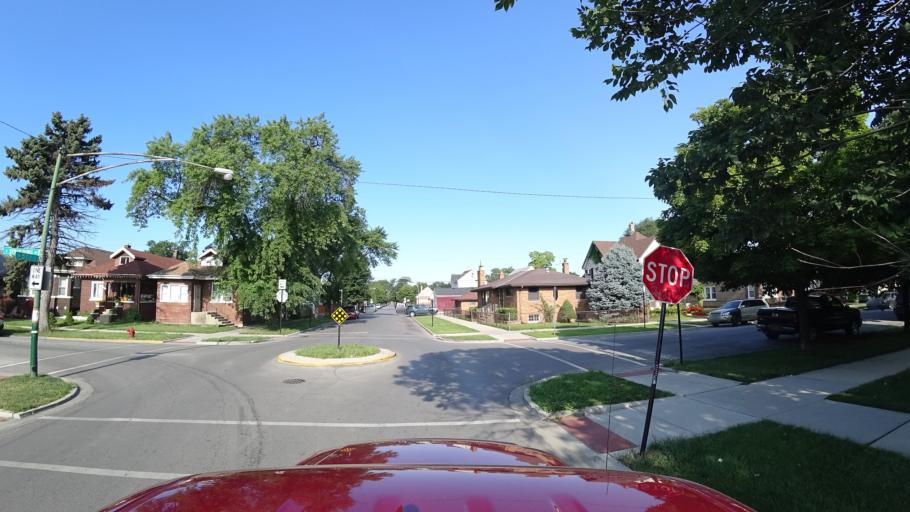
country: US
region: Illinois
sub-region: Cook County
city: Hometown
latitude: 41.7898
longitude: -87.7057
